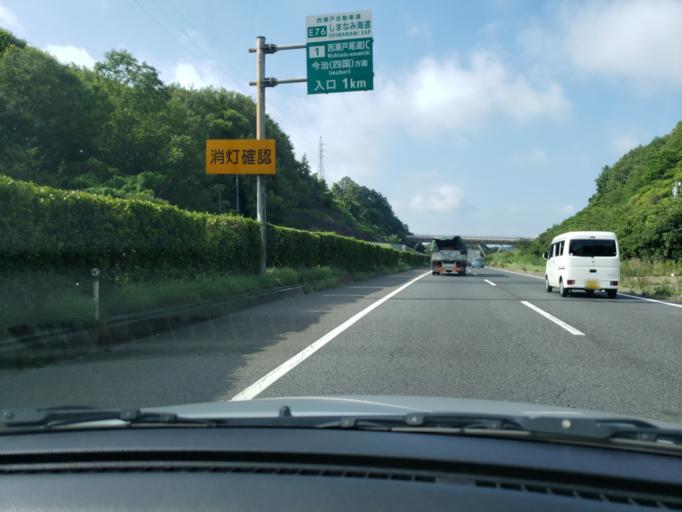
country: JP
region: Hiroshima
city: Onomichi
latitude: 34.4413
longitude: 133.2269
